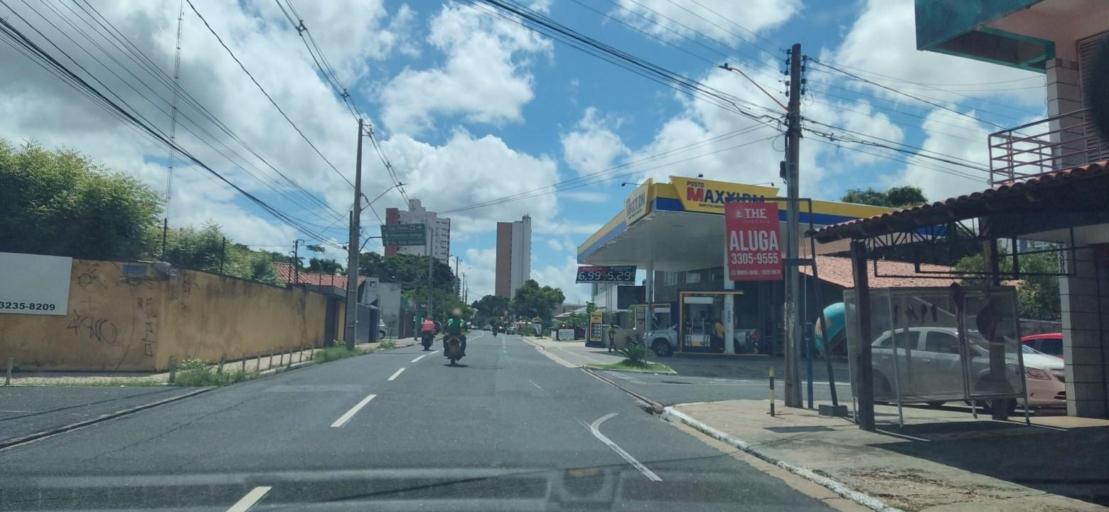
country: BR
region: Piaui
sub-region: Teresina
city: Teresina
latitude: -5.0639
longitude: -42.7903
